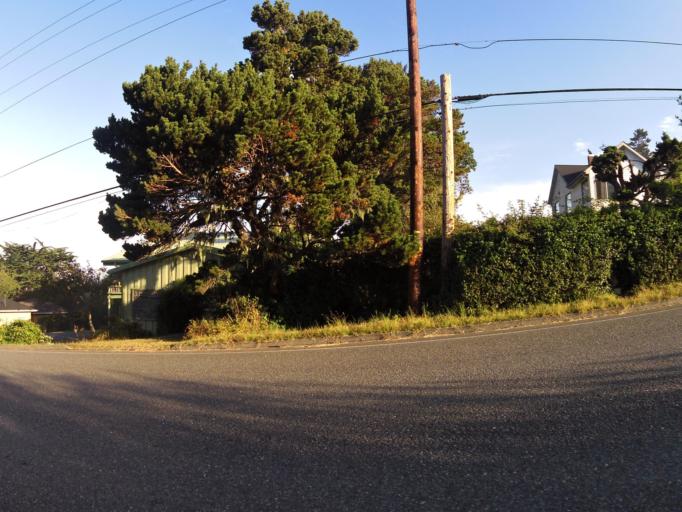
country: US
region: Oregon
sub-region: Curry County
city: Gold Beach
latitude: 42.4035
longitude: -124.4198
